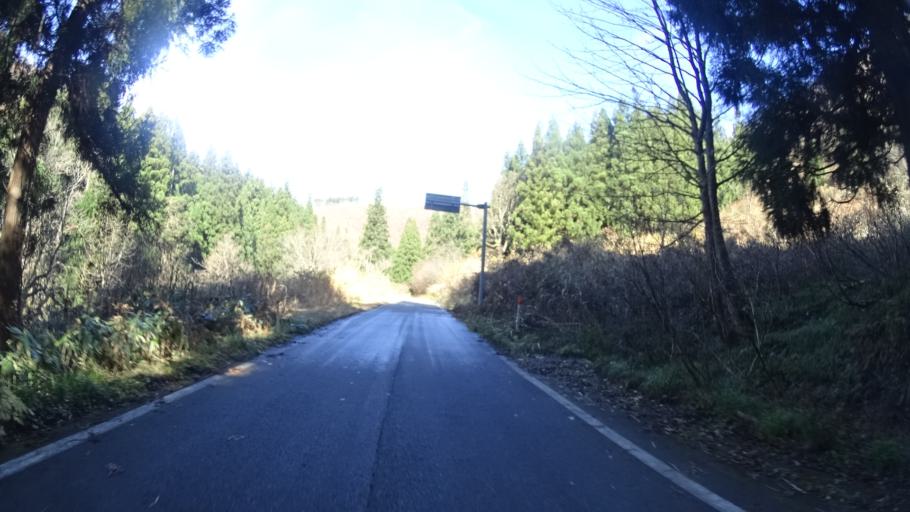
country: JP
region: Niigata
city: Muikamachi
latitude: 37.1745
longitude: 139.0862
